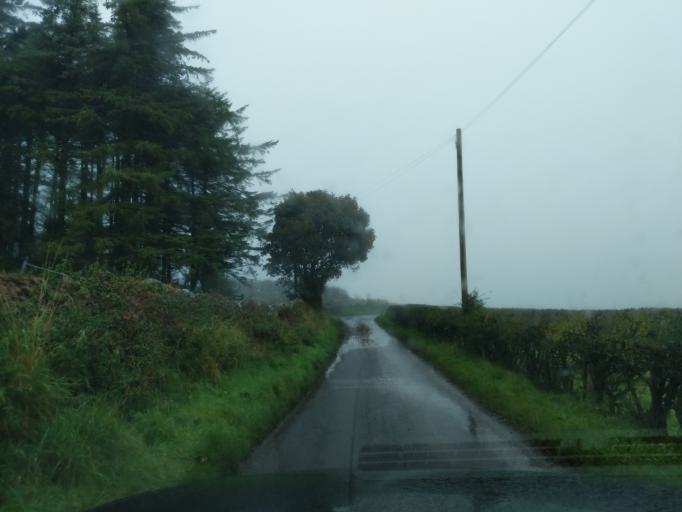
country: GB
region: Scotland
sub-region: East Lothian
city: Dunbar
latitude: 55.9334
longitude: -2.4285
